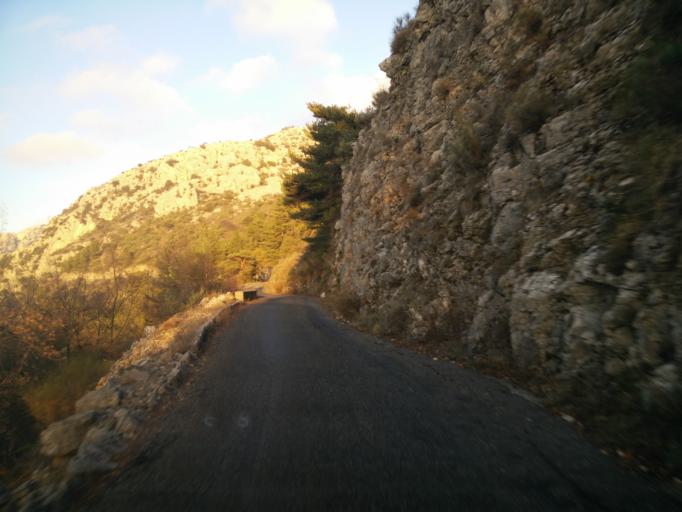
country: FR
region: Provence-Alpes-Cote d'Azur
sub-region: Departement des Alpes-Maritimes
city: Peille
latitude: 43.7944
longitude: 7.4047
